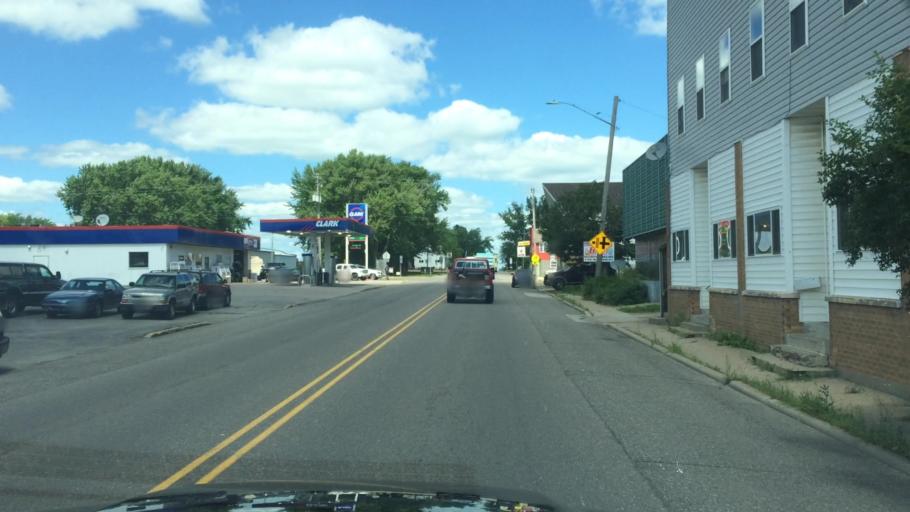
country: US
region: Wisconsin
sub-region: Taylor County
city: Medford
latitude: 45.0759
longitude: -90.3148
